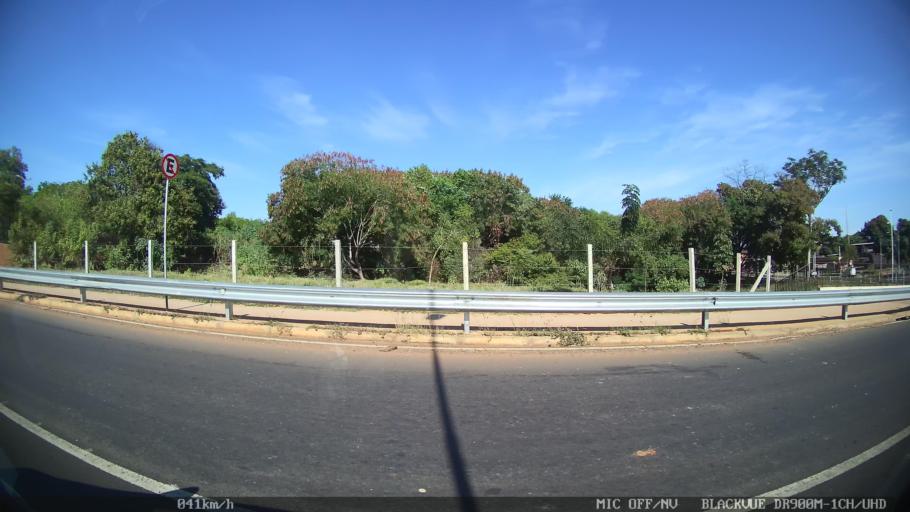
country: BR
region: Sao Paulo
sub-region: Sao Jose Do Rio Preto
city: Sao Jose do Rio Preto
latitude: -20.7899
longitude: -49.3902
